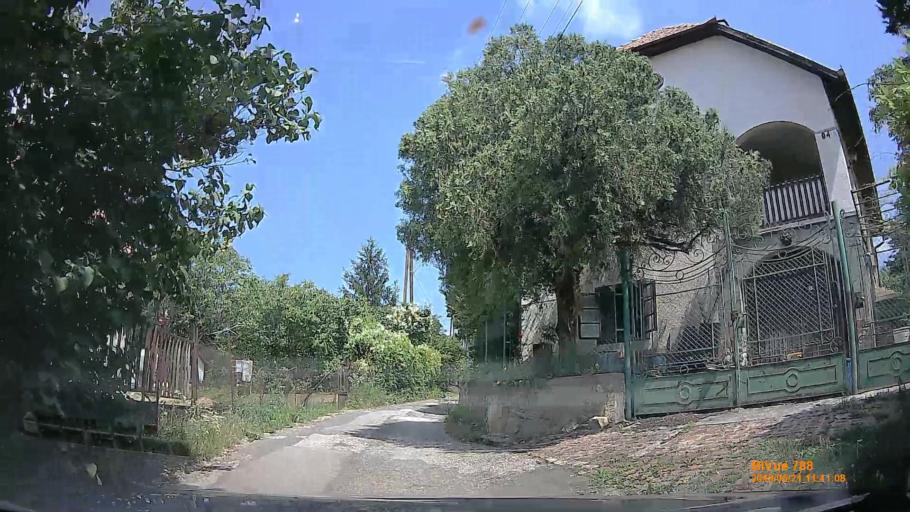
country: HU
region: Baranya
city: Pellerd
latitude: 46.0718
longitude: 18.1791
